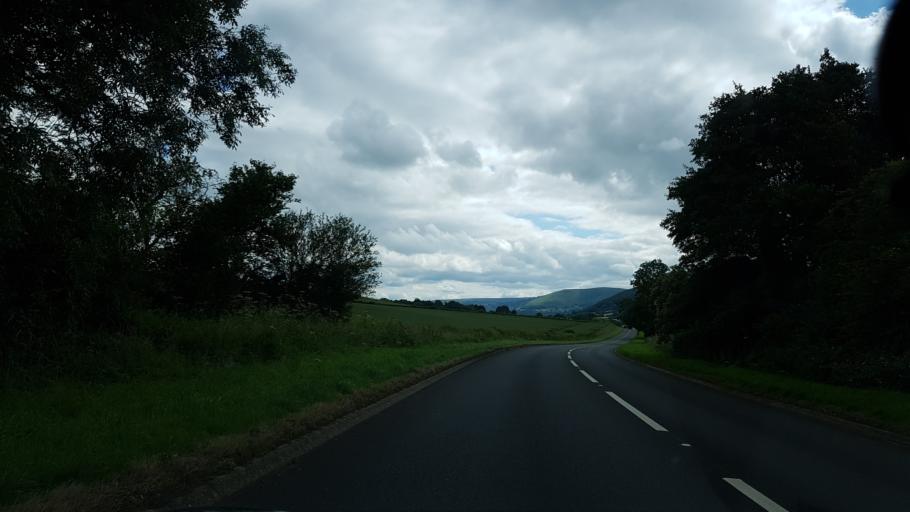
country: GB
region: Wales
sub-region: Monmouthshire
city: Abergavenny
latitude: 51.8675
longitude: -2.9901
